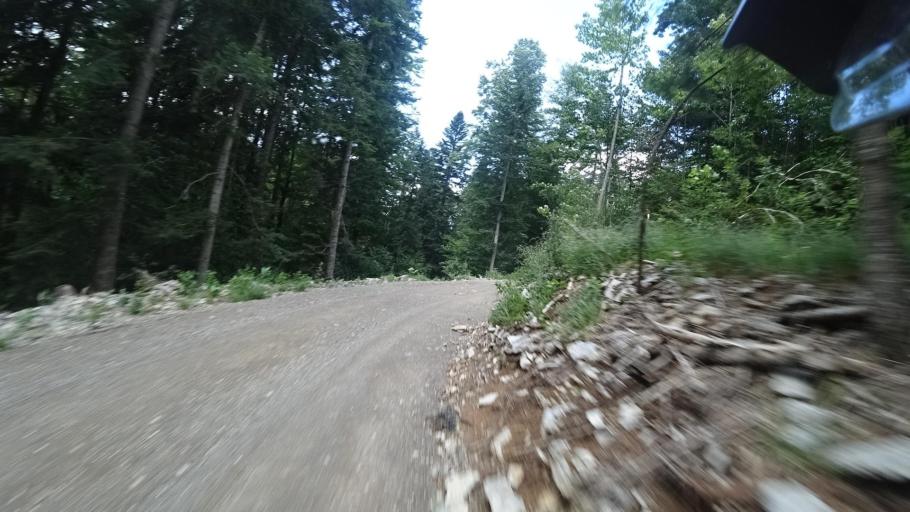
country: HR
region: Licko-Senjska
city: Senj
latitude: 45.1177
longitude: 14.9722
